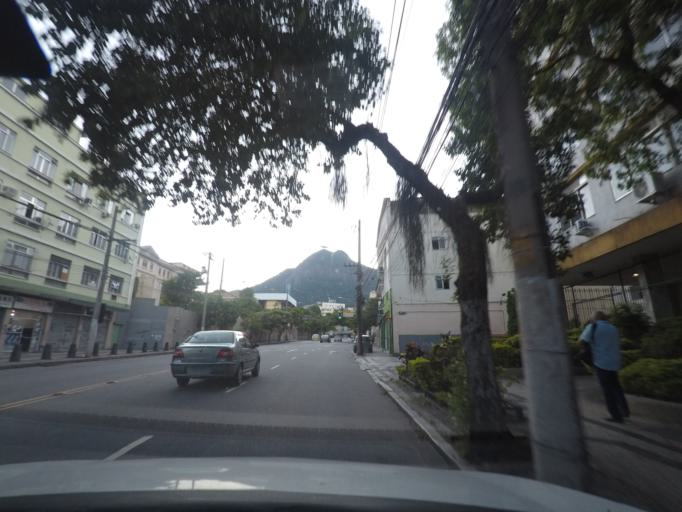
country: BR
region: Rio de Janeiro
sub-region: Rio De Janeiro
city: Rio de Janeiro
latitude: -22.9407
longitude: -43.2504
